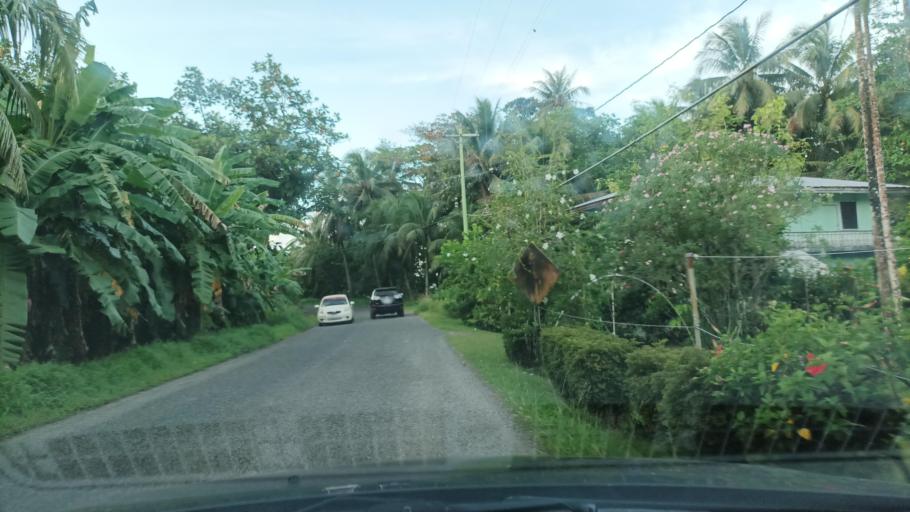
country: FM
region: Kosrae
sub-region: Lelu Municipality
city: Lelu
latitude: 5.3165
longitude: 163.0339
